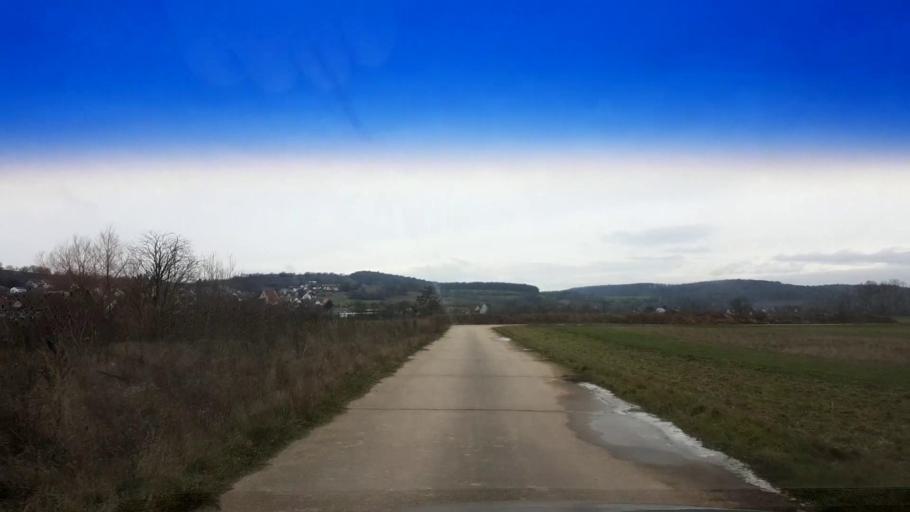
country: DE
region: Bavaria
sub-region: Upper Franconia
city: Viereth-Trunstadt
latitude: 49.9307
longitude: 10.7609
